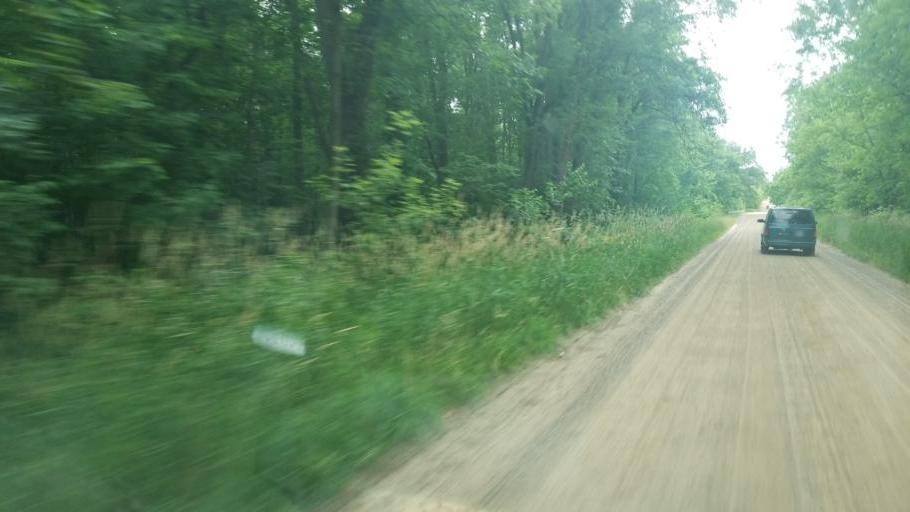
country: US
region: Michigan
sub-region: Barry County
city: Nashville
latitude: 42.6177
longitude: -84.9757
